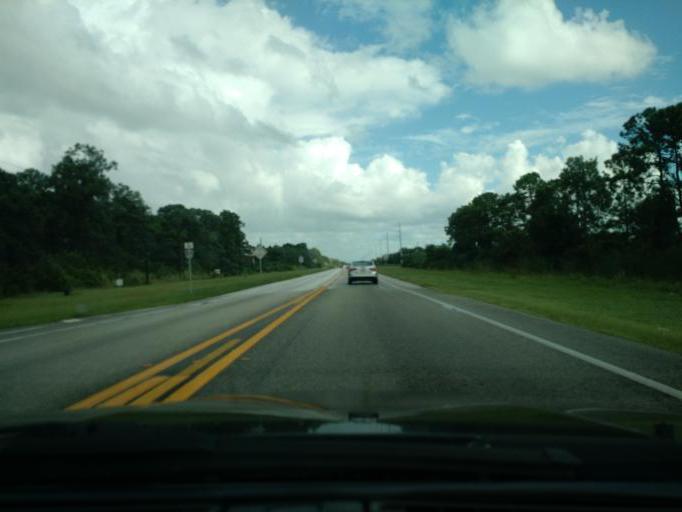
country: US
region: Florida
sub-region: Lee County
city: Gateway
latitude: 26.6131
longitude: -81.7615
